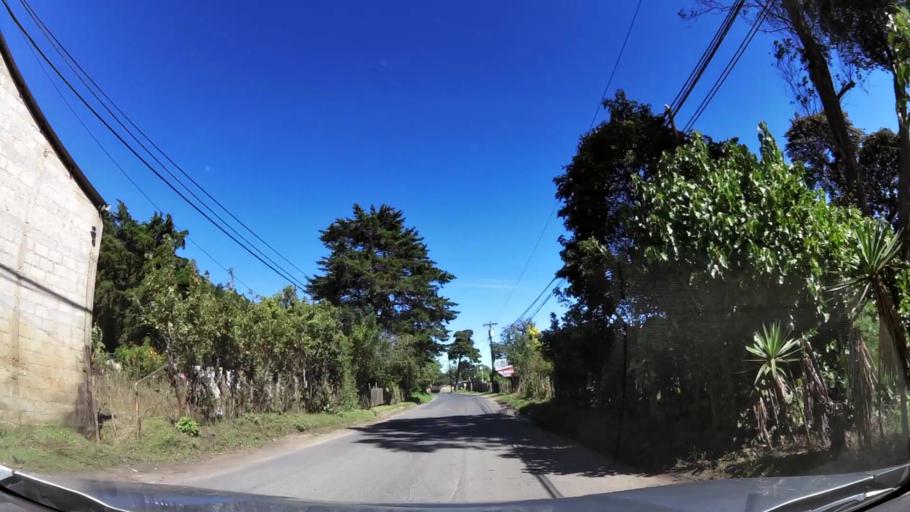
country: GT
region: Guatemala
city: San Jose Pinula
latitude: 14.5325
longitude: -90.4152
